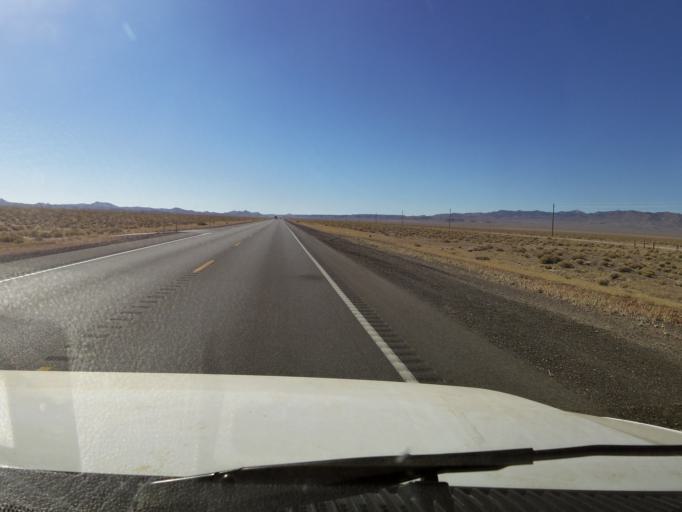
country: US
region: Nevada
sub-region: Esmeralda County
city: Goldfield
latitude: 37.8459
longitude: -117.2411
